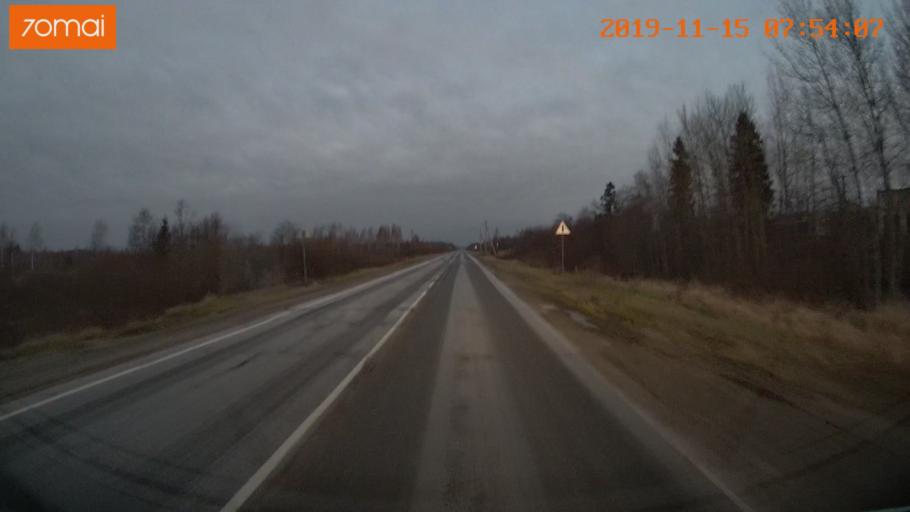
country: RU
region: Vologda
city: Cherepovets
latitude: 58.8955
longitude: 38.1795
